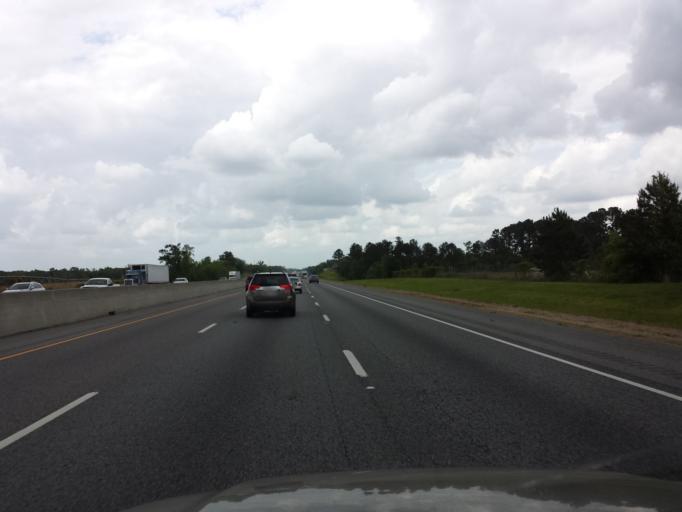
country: US
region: Georgia
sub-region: Lowndes County
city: Hahira
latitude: 30.9592
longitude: -83.3778
